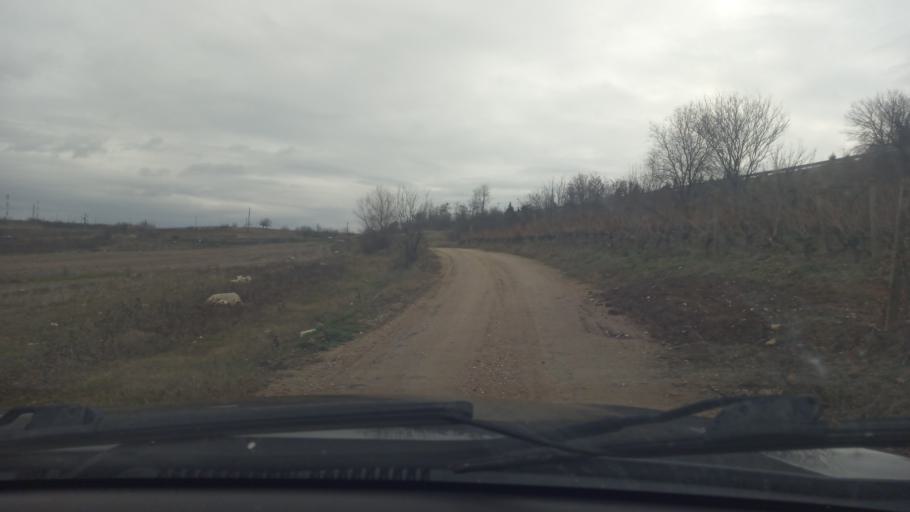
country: MK
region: Gradsko
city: Gradsko
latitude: 41.5755
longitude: 21.9333
